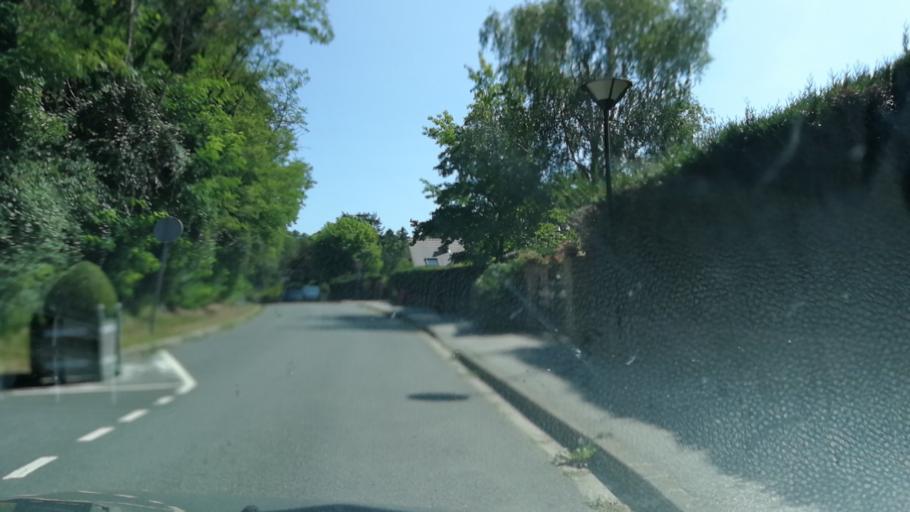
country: FR
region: Ile-de-France
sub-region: Departement des Yvelines
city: Chevreuse
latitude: 48.7054
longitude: 2.0538
